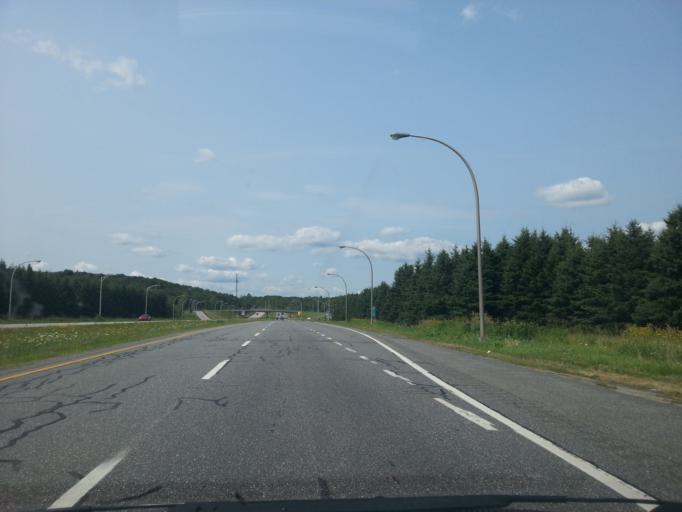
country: CA
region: Quebec
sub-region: Outaouais
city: Gatineau
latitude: 45.4987
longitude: -75.7996
